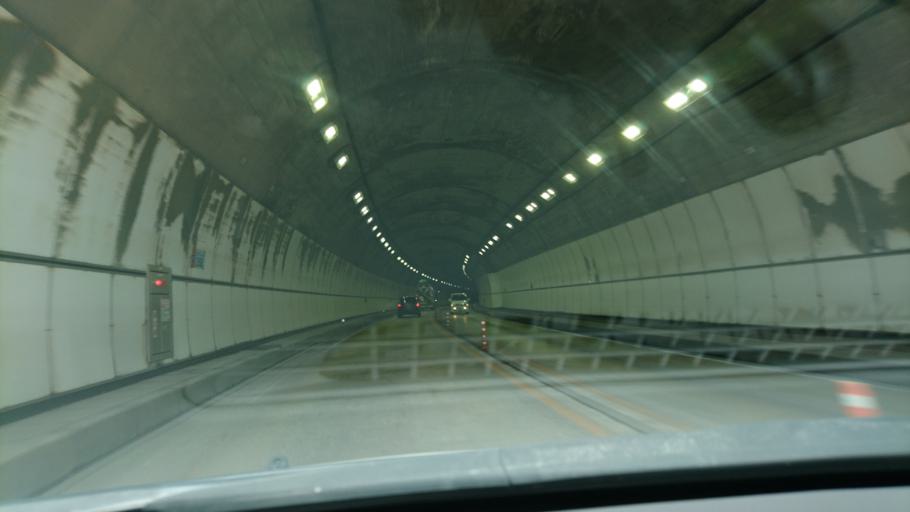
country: JP
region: Aomori
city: Hachinohe
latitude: 40.2027
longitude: 141.7817
